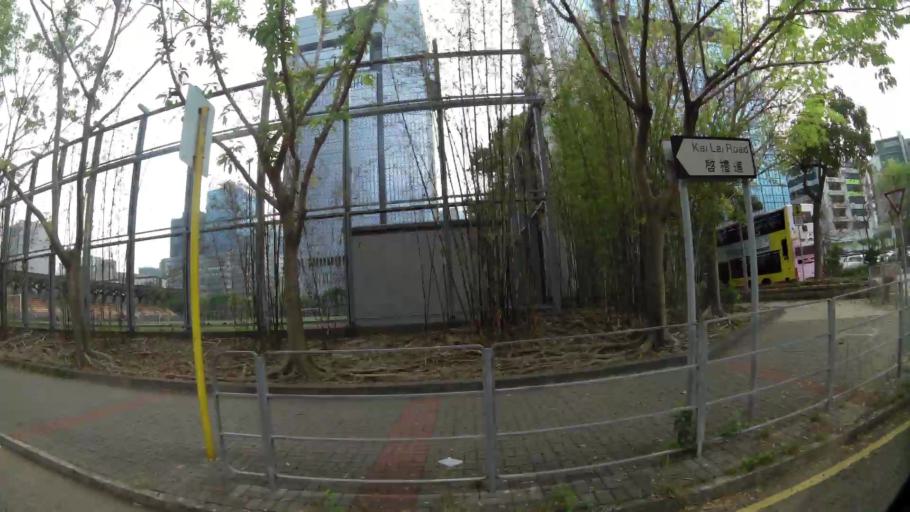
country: HK
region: Kowloon City
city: Kowloon
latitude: 22.3274
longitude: 114.2060
